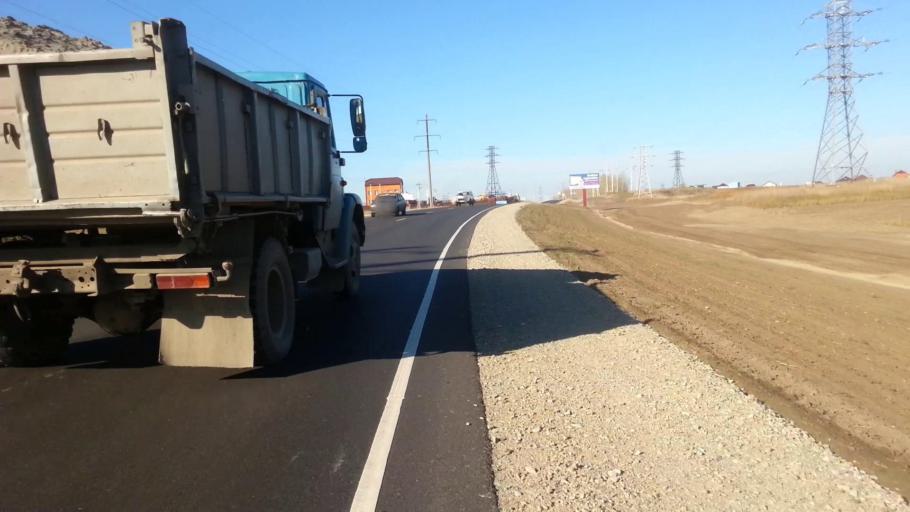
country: RU
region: Altai Krai
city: Sannikovo
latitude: 53.3332
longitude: 83.9381
